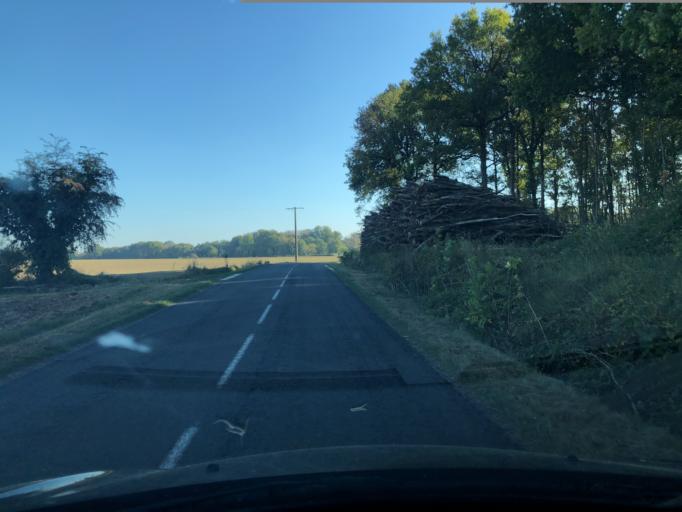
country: FR
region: Centre
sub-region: Departement d'Indre-et-Loire
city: Neuvy-le-Roi
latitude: 47.5738
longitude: 0.5991
